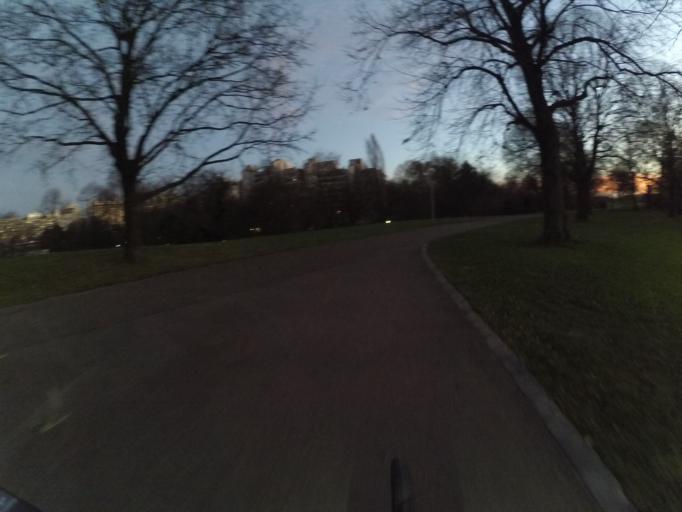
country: DE
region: Bavaria
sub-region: Upper Bavaria
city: Munich
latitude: 48.1844
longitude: 11.5469
